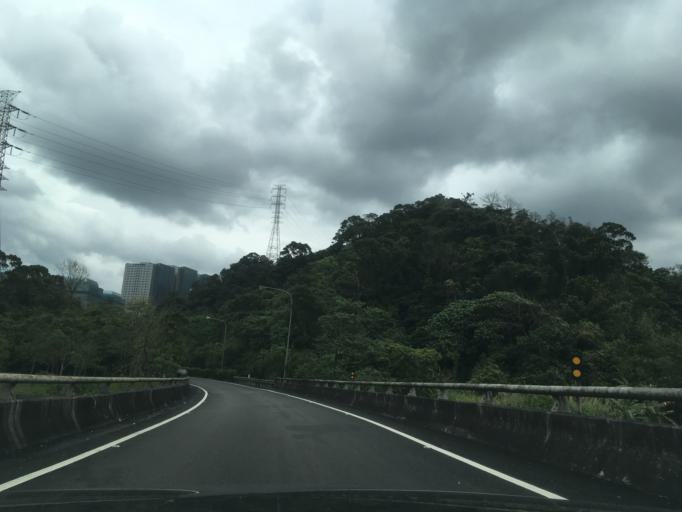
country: TW
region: Taipei
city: Taipei
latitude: 25.0557
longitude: 121.6405
